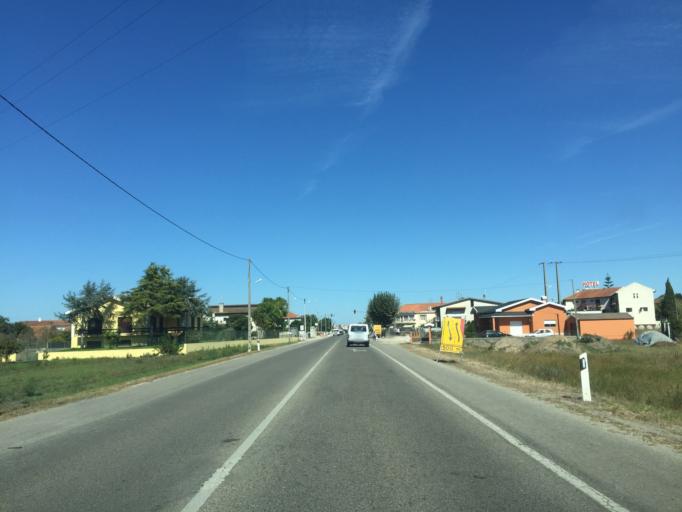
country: PT
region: Coimbra
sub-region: Montemor-O-Velho
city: Arazede
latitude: 40.3047
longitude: -8.7581
